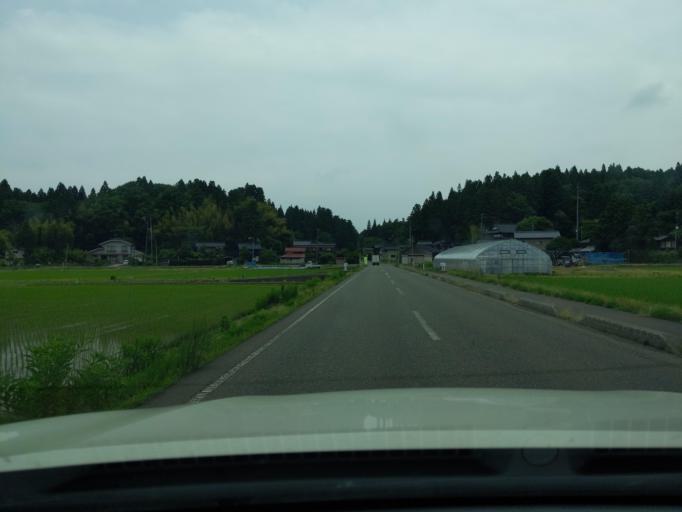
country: JP
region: Niigata
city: Kashiwazaki
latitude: 37.3425
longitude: 138.5853
